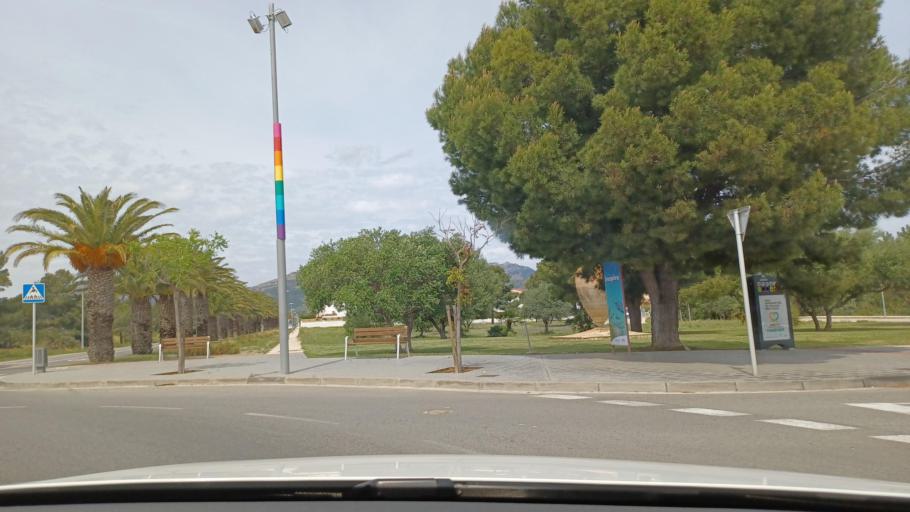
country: ES
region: Catalonia
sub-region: Provincia de Tarragona
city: Colldejou
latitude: 41.0191
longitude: 0.9398
